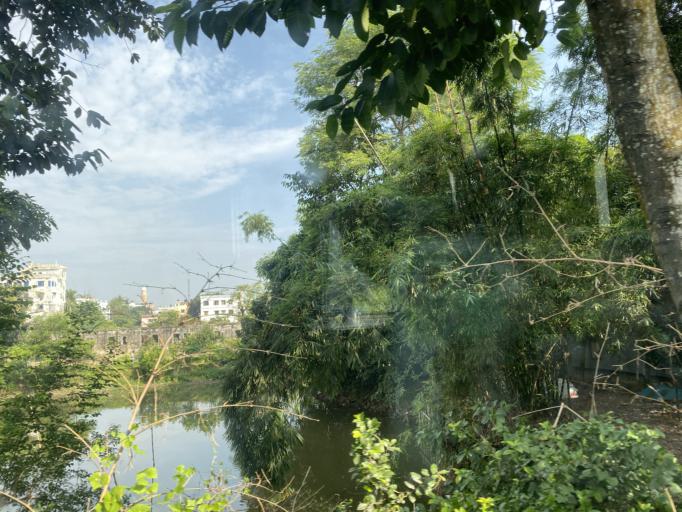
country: BD
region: Dhaka
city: Bhairab Bazar
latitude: 23.9679
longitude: 91.1140
